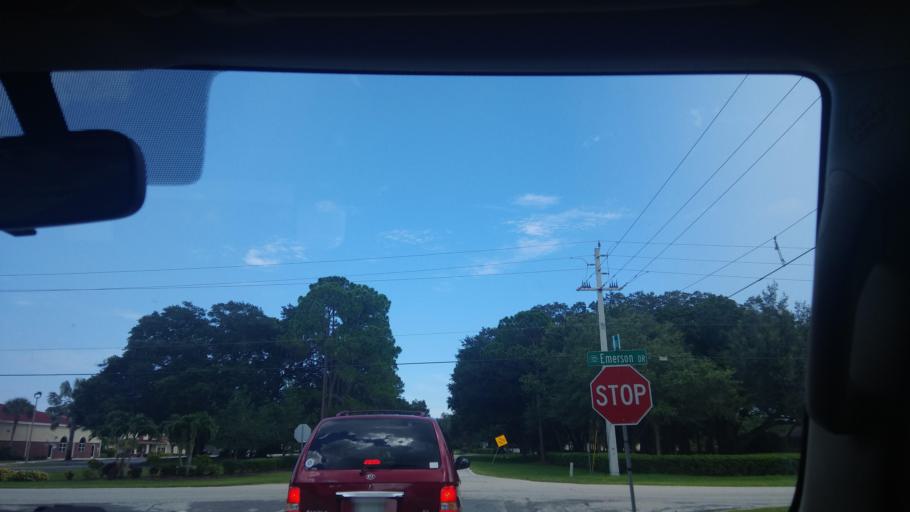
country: US
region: Florida
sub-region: Brevard County
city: West Melbourne
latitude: 28.0099
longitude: -80.6459
